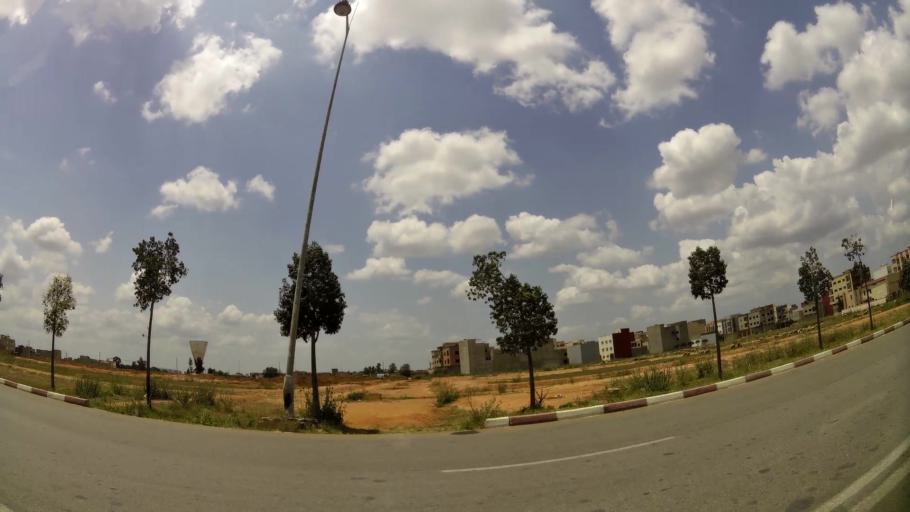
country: MA
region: Rabat-Sale-Zemmour-Zaer
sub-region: Khemisset
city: Tiflet
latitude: 34.0044
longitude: -6.5231
